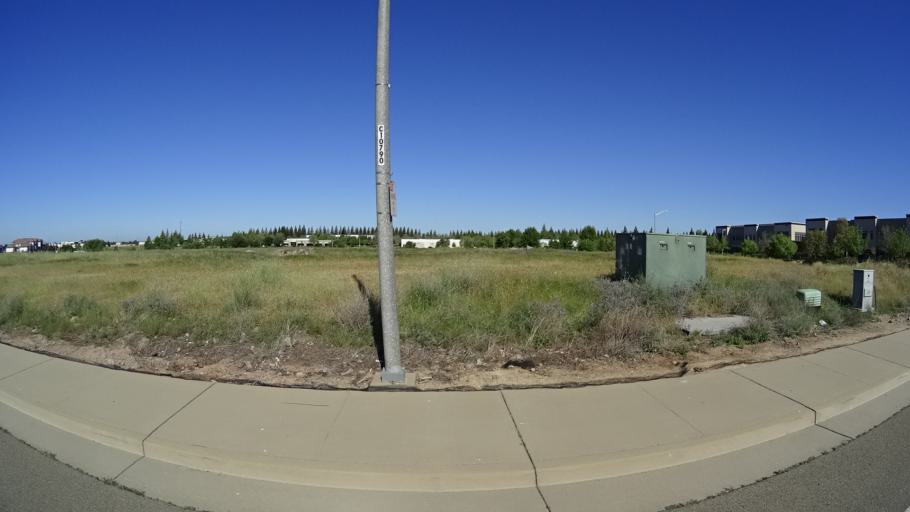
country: US
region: California
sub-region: Placer County
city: Roseville
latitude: 38.8114
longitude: -121.2924
